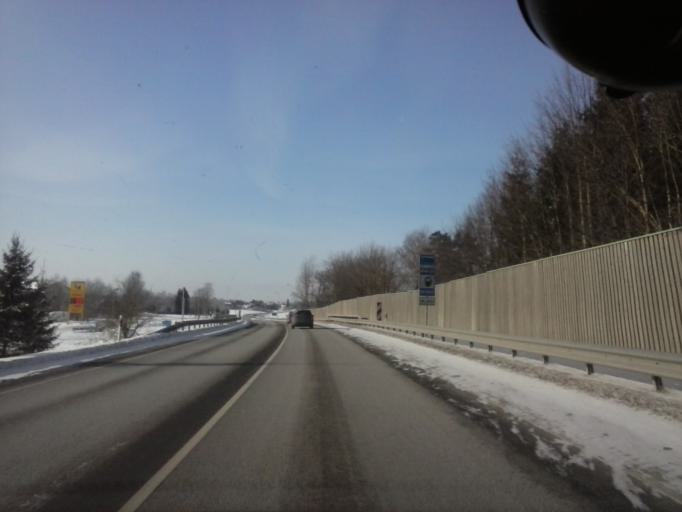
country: EE
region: Tartu
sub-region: Tartu linn
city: Tartu
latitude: 58.3572
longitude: 26.6221
